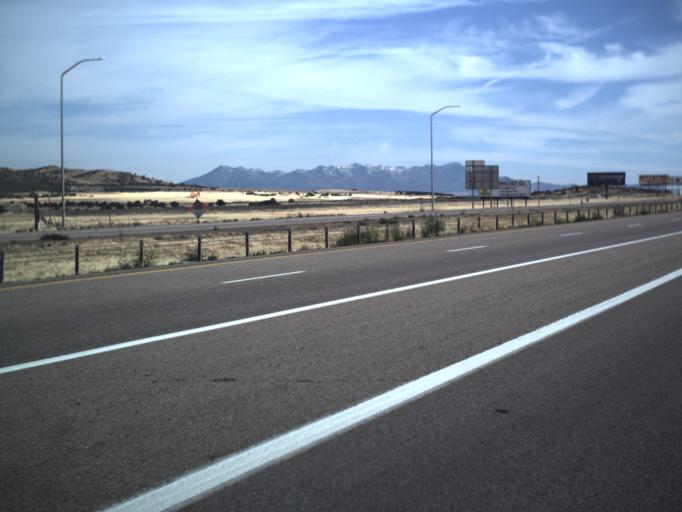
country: US
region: Utah
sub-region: Millard County
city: Fillmore
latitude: 38.9947
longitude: -112.3208
